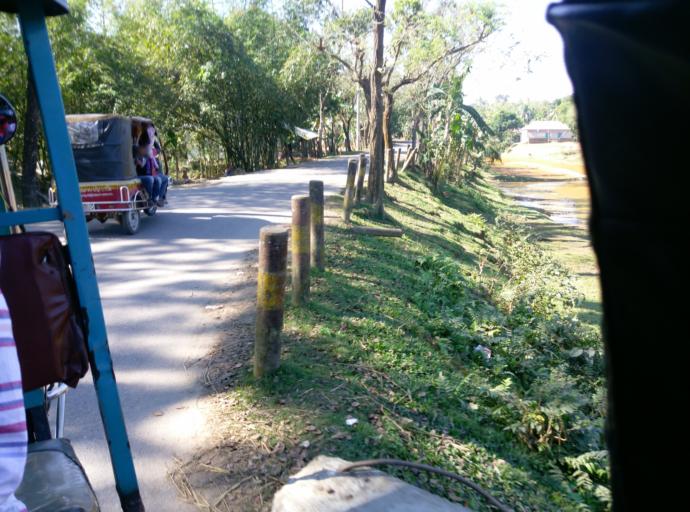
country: BD
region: Dhaka
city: Netrakona
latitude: 25.0683
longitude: 90.5037
